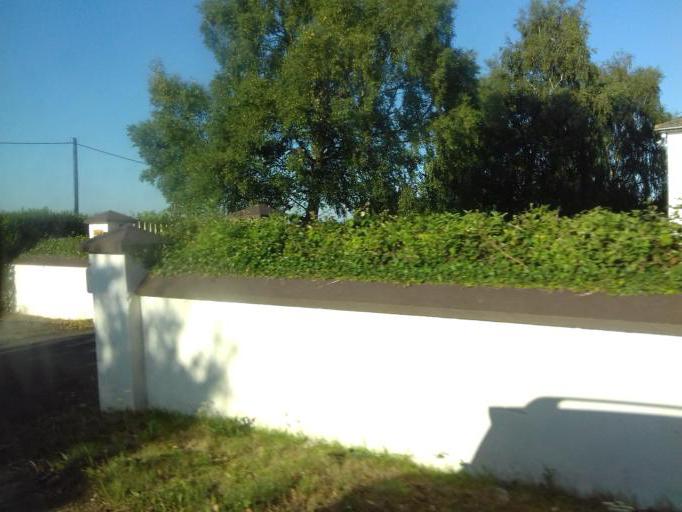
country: IE
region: Leinster
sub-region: An Mhi
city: Ashbourne
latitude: 53.4865
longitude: -6.3169
